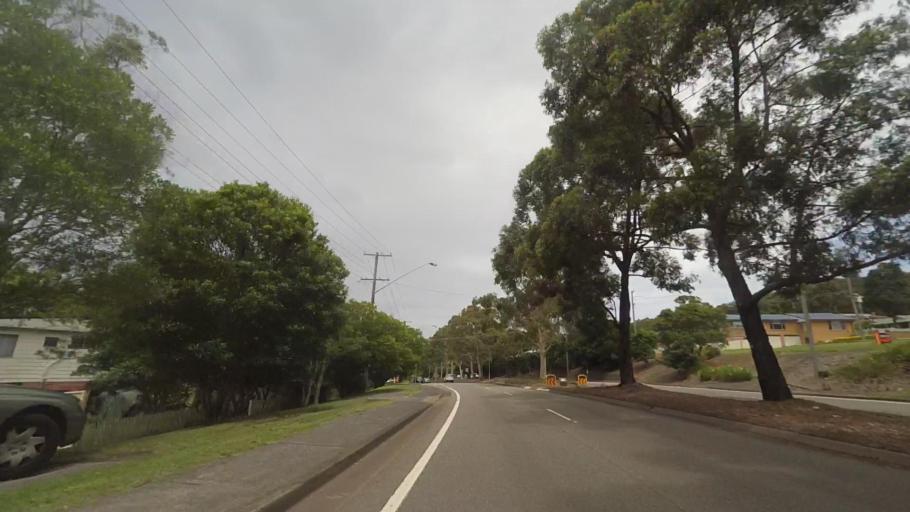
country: AU
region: New South Wales
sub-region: Wyong Shire
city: Berkeley Vale
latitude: -33.3522
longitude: 151.4342
